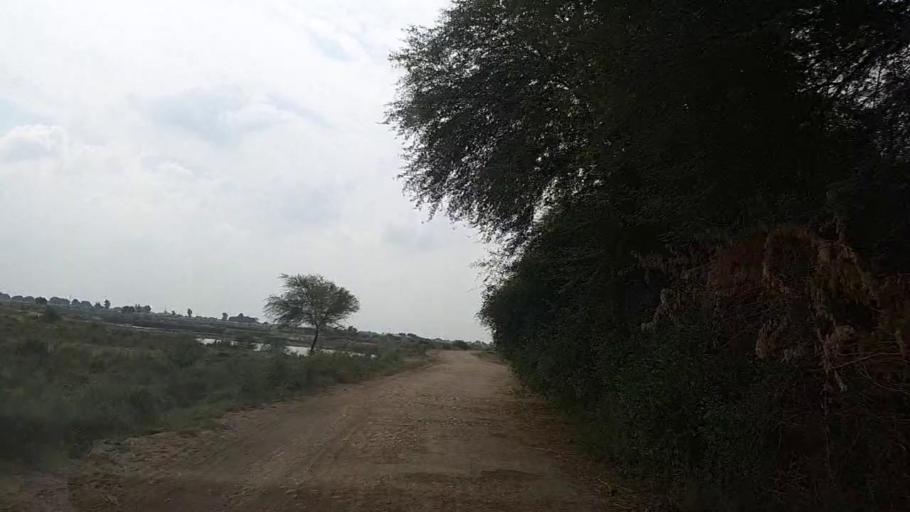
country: PK
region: Sindh
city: Mirpur Batoro
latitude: 24.5877
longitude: 68.1233
